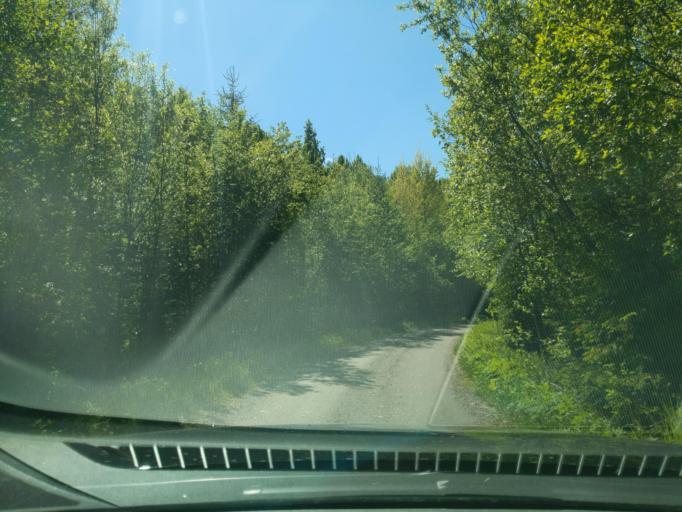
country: FI
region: Paijanne Tavastia
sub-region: Lahti
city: Lahti
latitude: 61.0589
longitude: 25.7014
